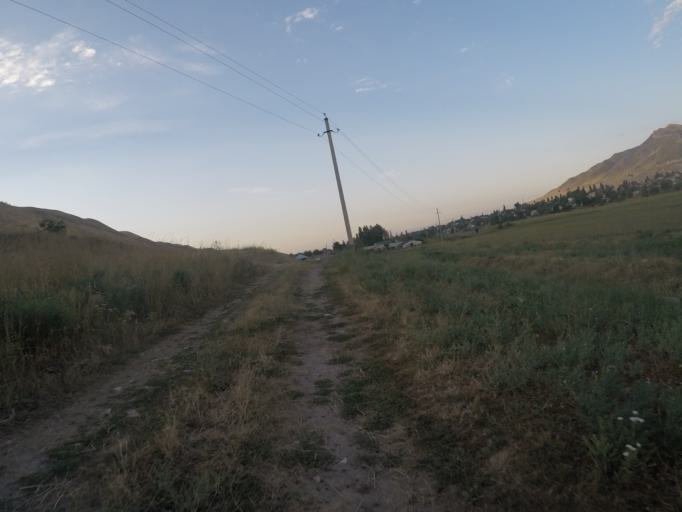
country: KG
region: Chuy
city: Bishkek
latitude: 42.7624
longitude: 74.6372
